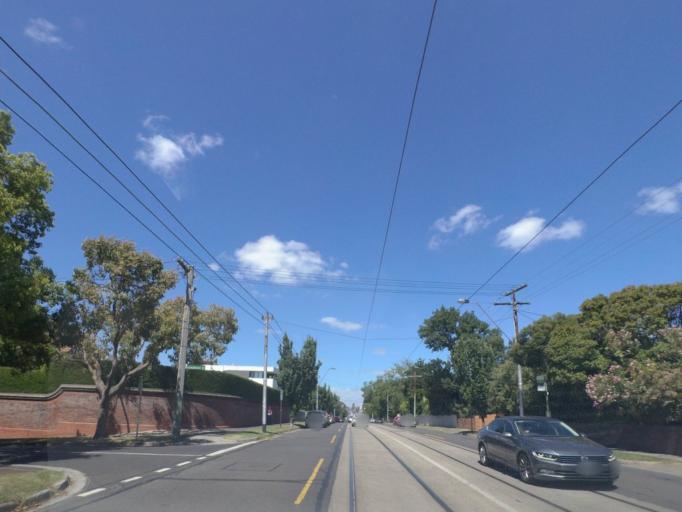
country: AU
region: Victoria
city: Balwyn
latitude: -37.8118
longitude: 145.0717
